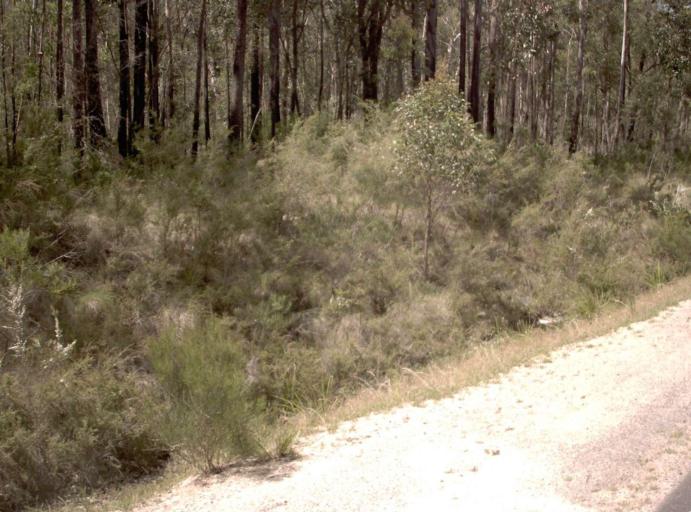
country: AU
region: New South Wales
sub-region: Bombala
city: Bombala
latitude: -37.5458
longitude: 149.4365
